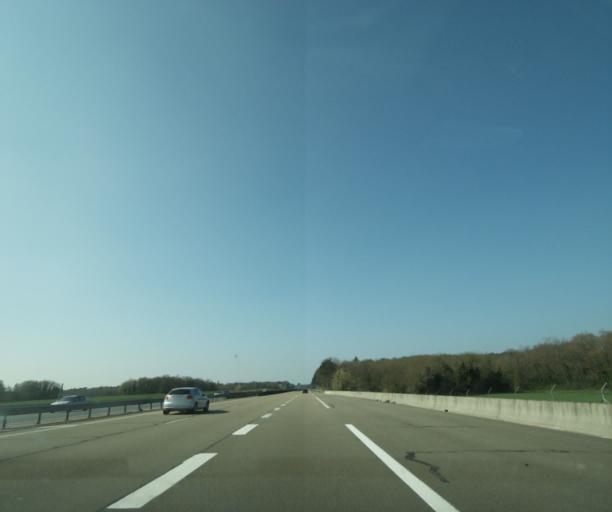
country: FR
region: Ile-de-France
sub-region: Departement de Seine-et-Marne
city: Souppes-sur-Loing
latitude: 48.2294
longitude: 2.7602
